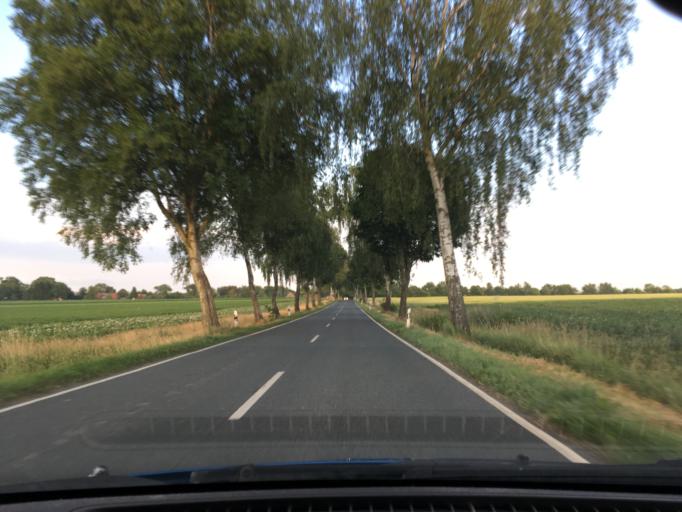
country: DE
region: Lower Saxony
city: Scharnhorst
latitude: 52.7205
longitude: 10.3050
